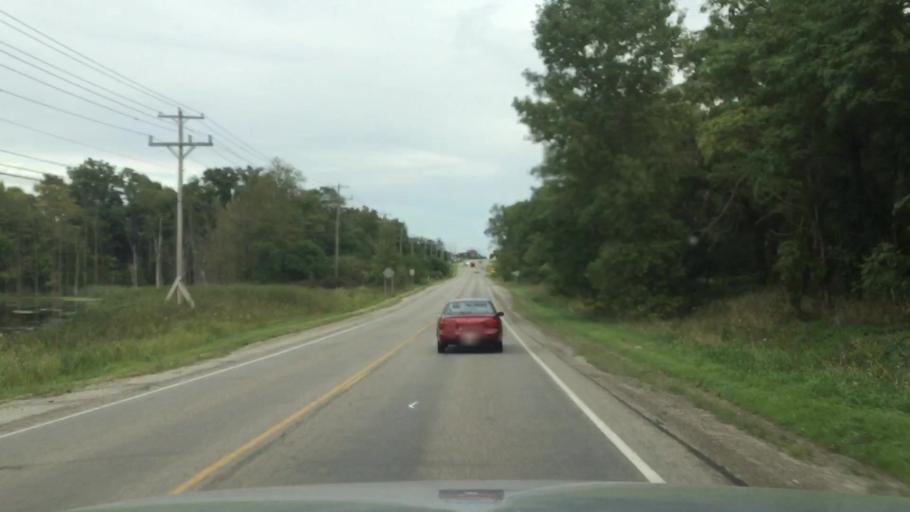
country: US
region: Michigan
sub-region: Genesee County
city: Grand Blanc
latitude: 42.8867
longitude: -83.6377
